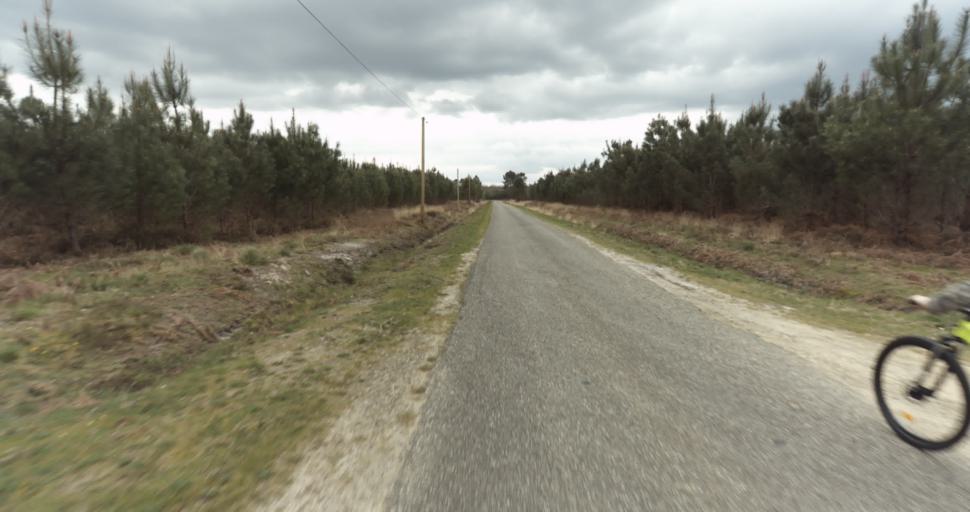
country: FR
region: Aquitaine
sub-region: Departement des Landes
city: Sarbazan
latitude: 44.0085
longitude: -0.3368
